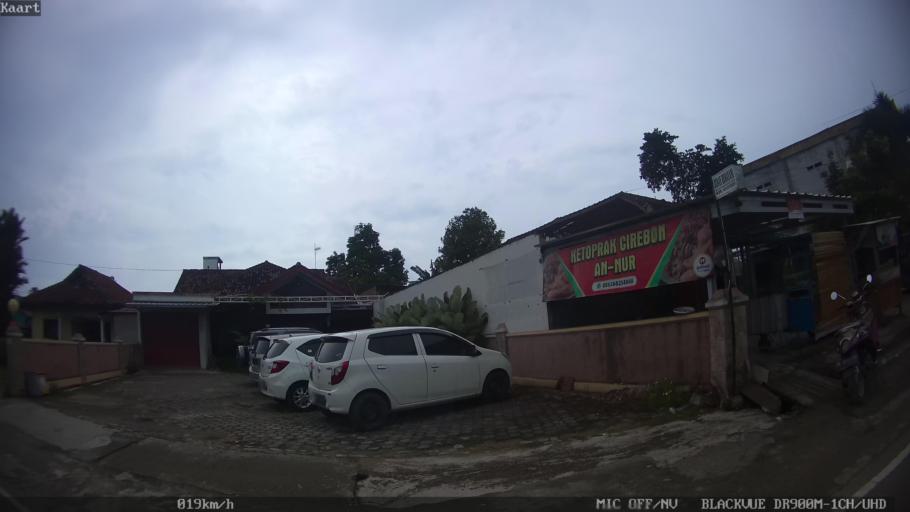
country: ID
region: Lampung
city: Kedaton
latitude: -5.3825
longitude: 105.2336
